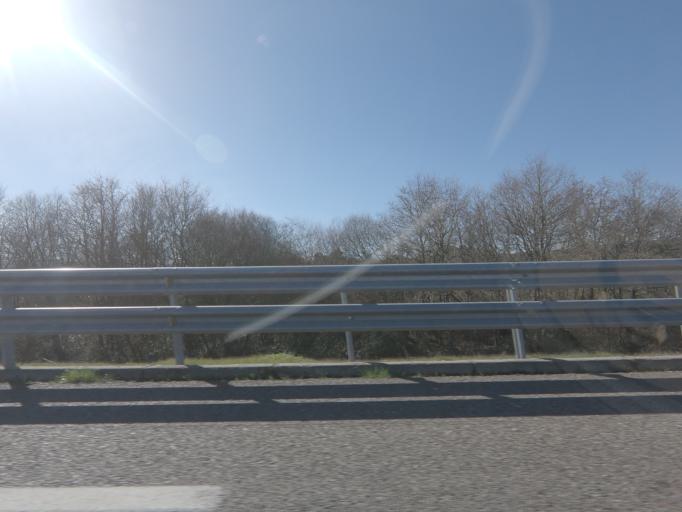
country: ES
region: Galicia
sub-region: Provincia de Ourense
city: Xinzo de Limia
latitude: 42.1019
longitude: -7.7316
